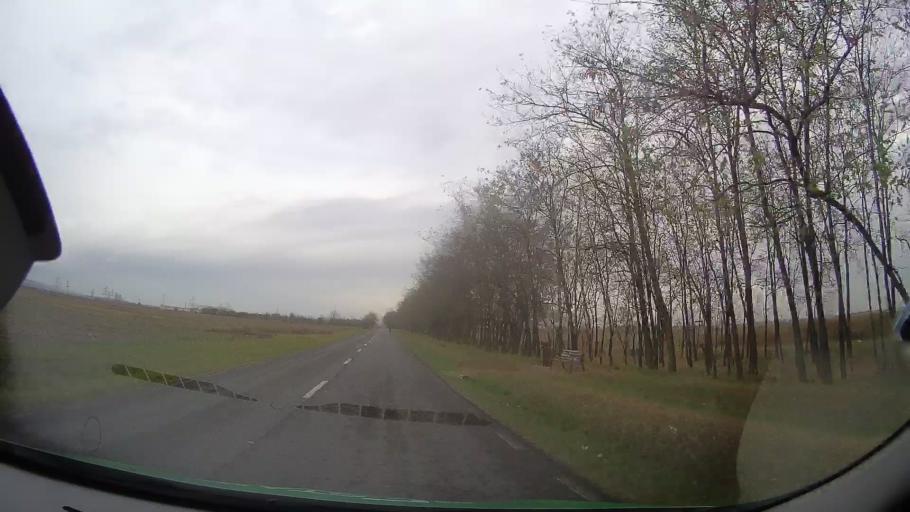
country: RO
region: Prahova
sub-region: Comuna Berceni
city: Berceni
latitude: 44.9396
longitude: 26.1086
